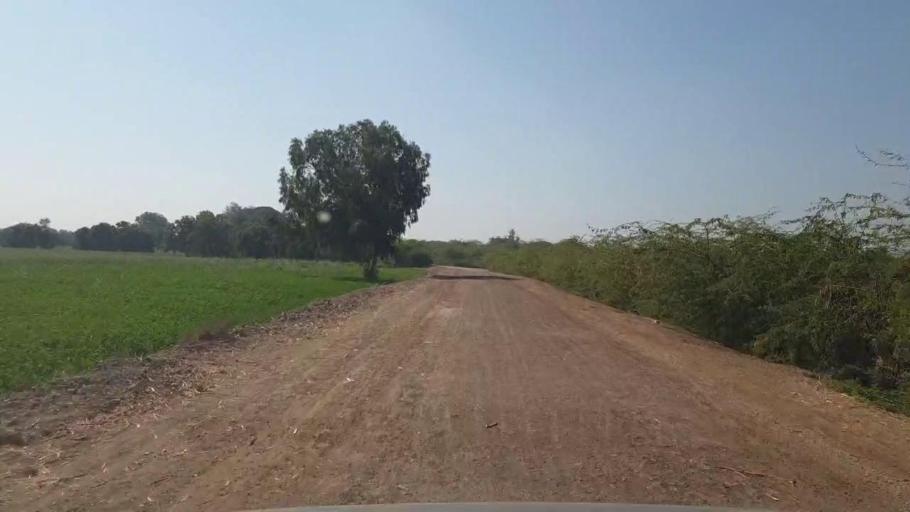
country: PK
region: Sindh
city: Digri
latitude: 25.2662
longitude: 69.2055
